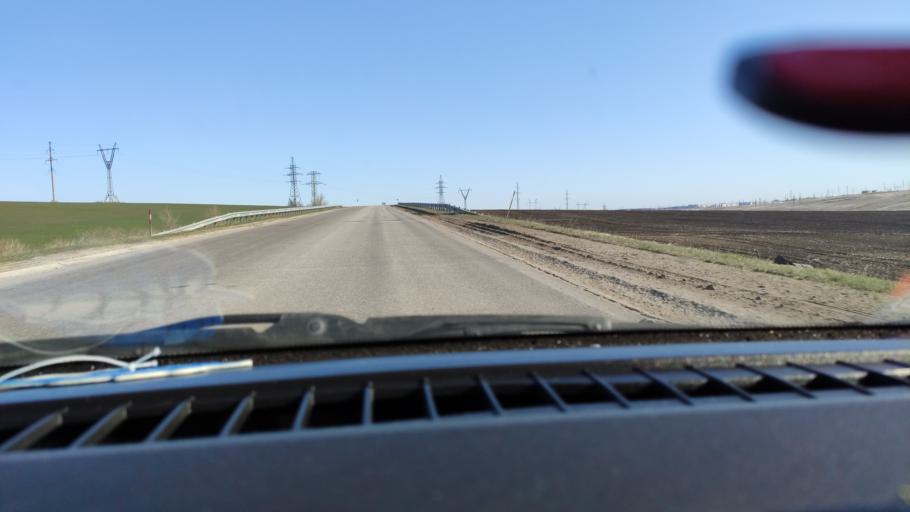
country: RU
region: Samara
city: Varlamovo
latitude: 53.0783
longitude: 48.3542
